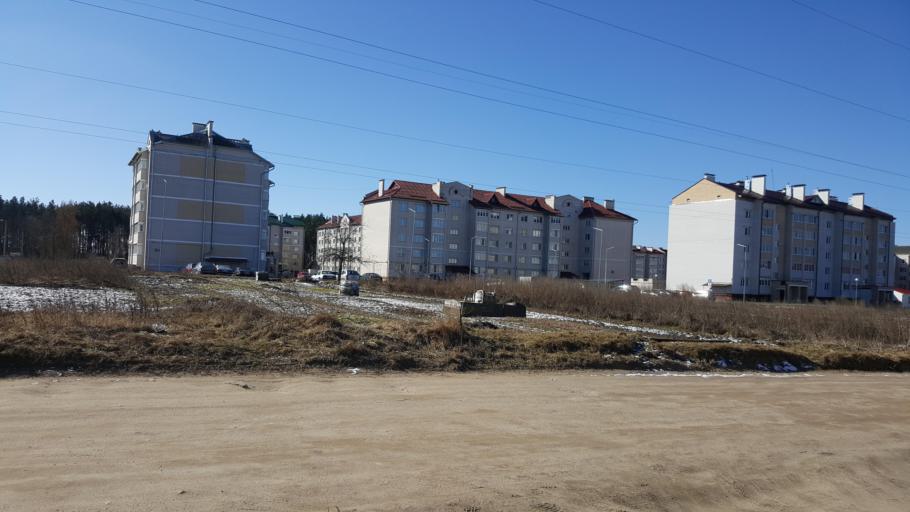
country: BY
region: Brest
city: Kamyanyets
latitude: 52.3912
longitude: 23.8260
